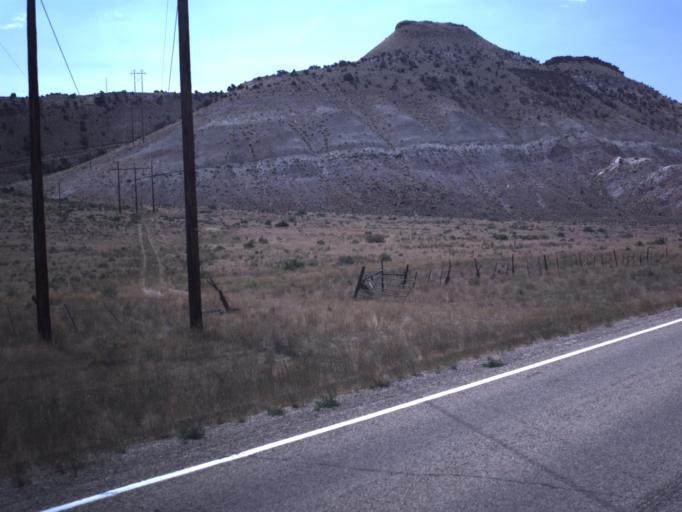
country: US
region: Utah
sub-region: Uintah County
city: Vernal
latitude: 40.5602
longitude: -109.5086
